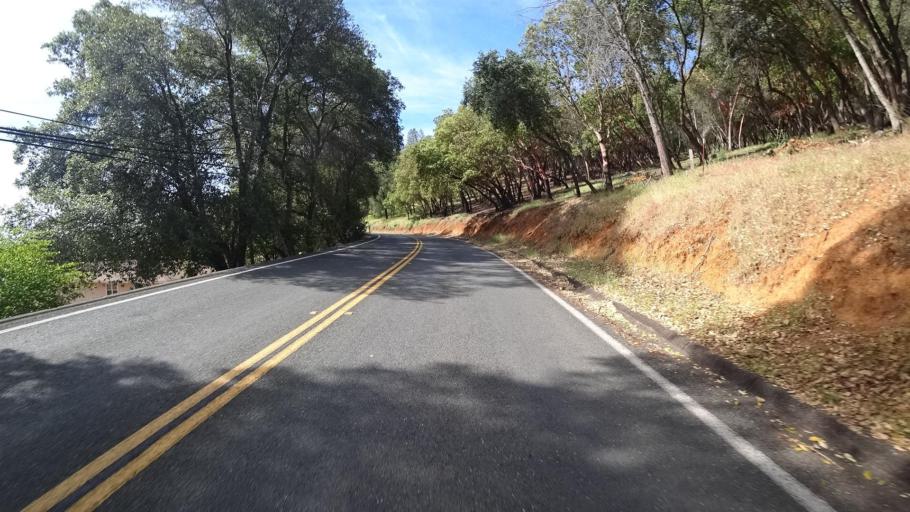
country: US
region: California
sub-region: Lake County
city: Soda Bay
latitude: 38.9980
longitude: -122.7529
